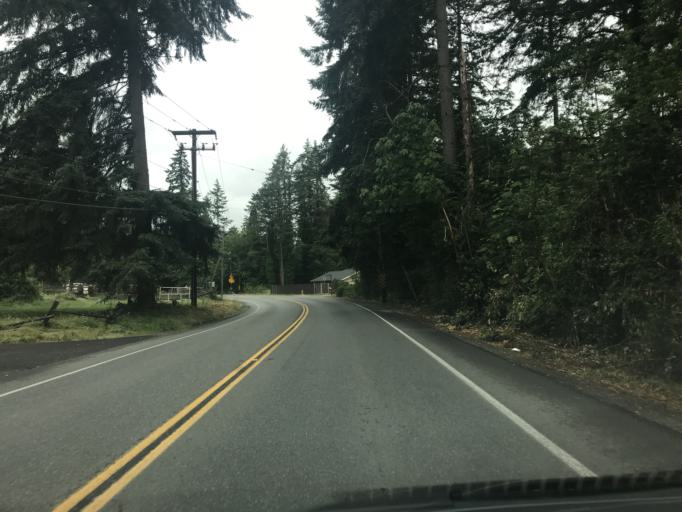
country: US
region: Washington
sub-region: King County
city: Covington
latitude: 47.3480
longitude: -122.1094
